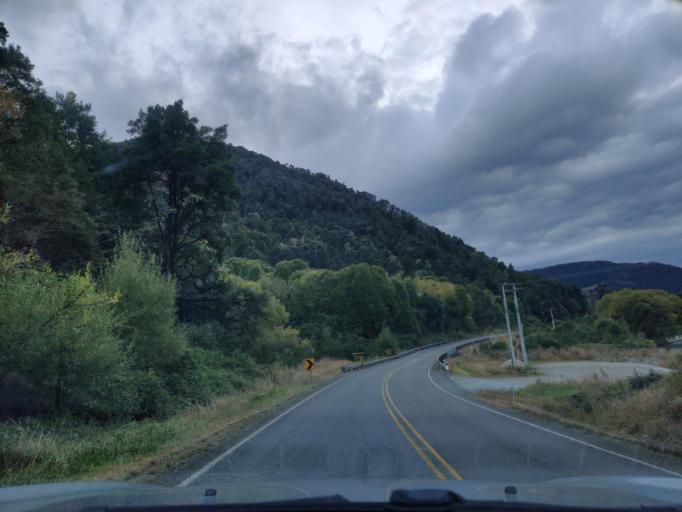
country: NZ
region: Tasman
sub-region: Tasman District
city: Wakefield
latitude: -41.6851
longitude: 172.4376
